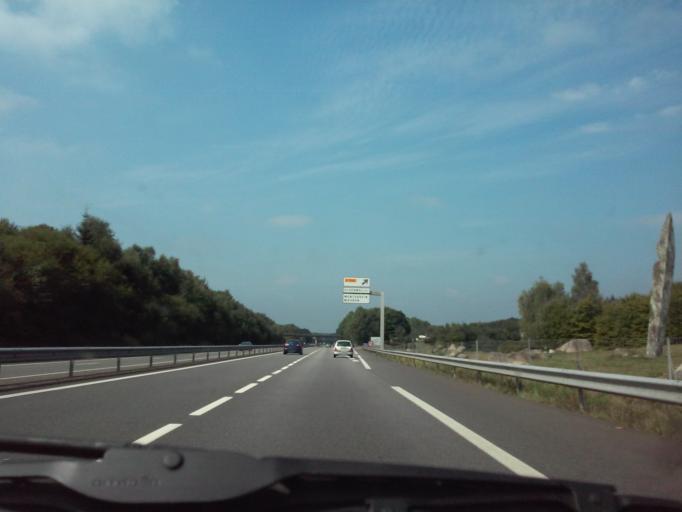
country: FR
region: Brittany
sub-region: Departement du Morbihan
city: Ploermel
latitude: 47.9184
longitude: -2.3823
